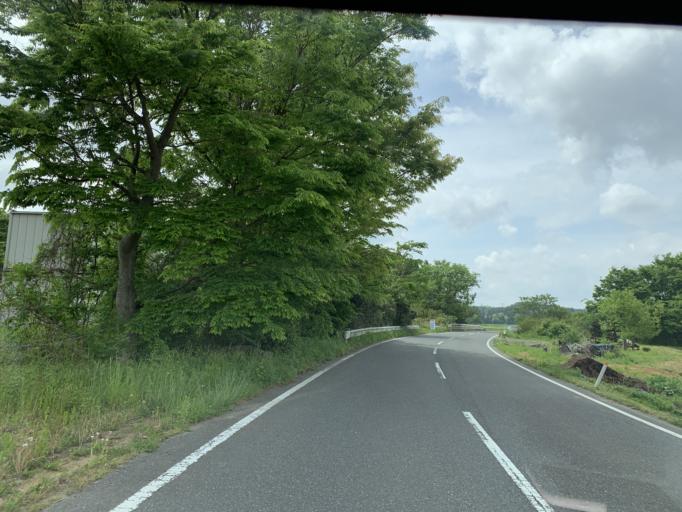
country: JP
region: Iwate
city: Ichinoseki
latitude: 38.8259
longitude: 141.0211
